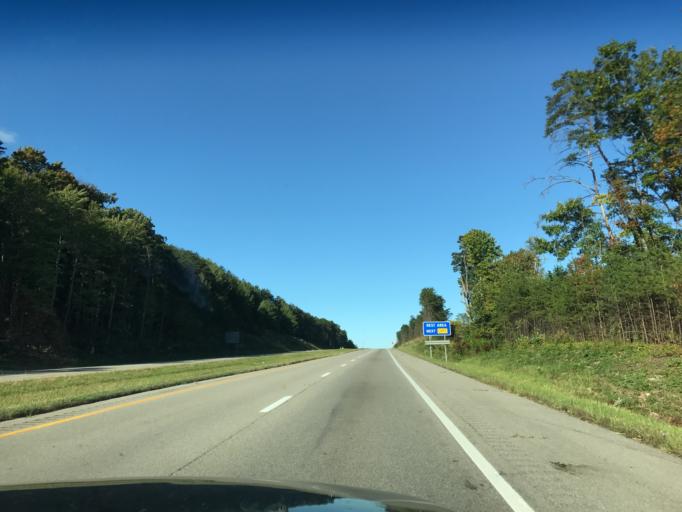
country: US
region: West Virginia
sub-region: Wood County
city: Washington
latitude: 39.2368
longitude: -81.7505
